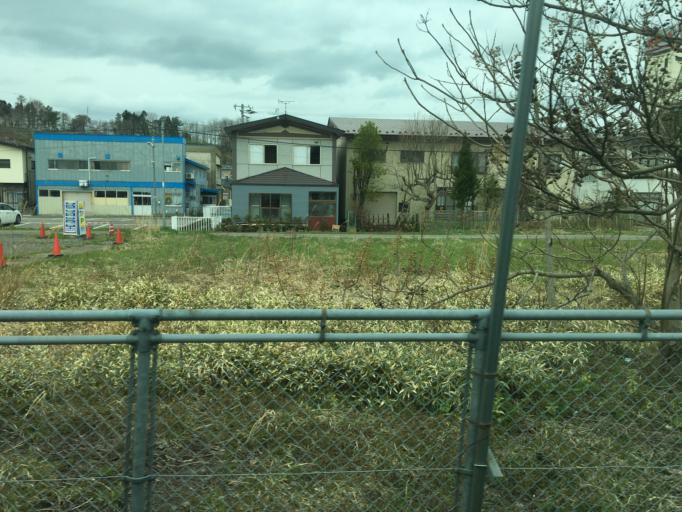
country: JP
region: Aomori
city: Shimokizukuri
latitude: 40.7748
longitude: 140.2200
